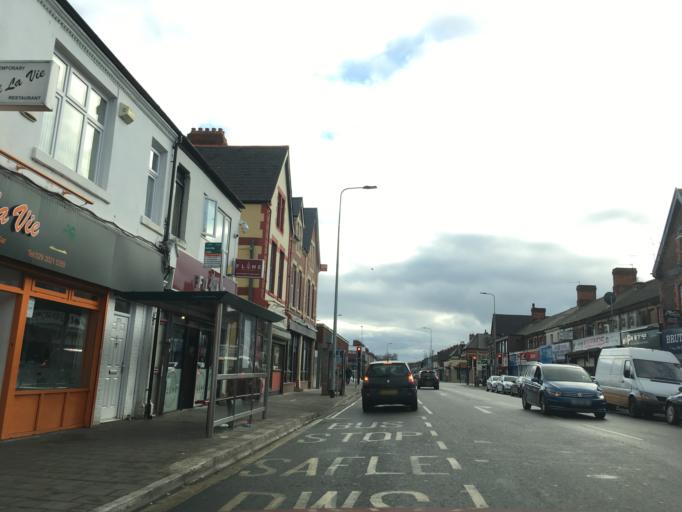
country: GB
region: Wales
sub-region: Cardiff
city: Cardiff
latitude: 51.4710
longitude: -3.1864
